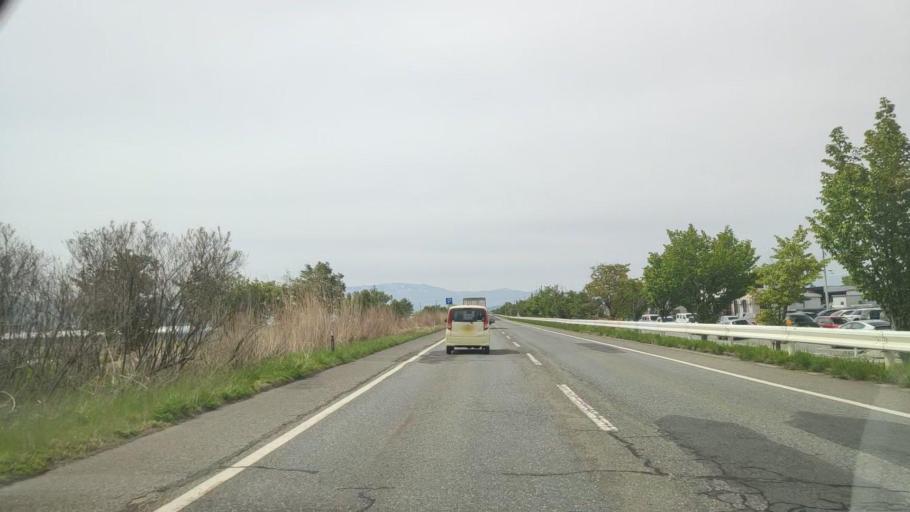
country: JP
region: Yamagata
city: Takahata
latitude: 38.0435
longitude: 140.1750
